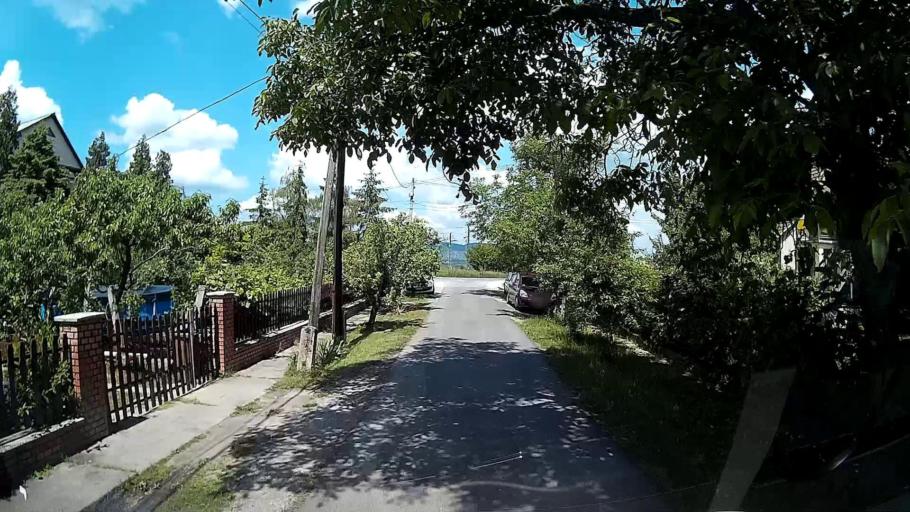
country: HU
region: Pest
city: Pomaz
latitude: 47.6458
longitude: 19.0376
